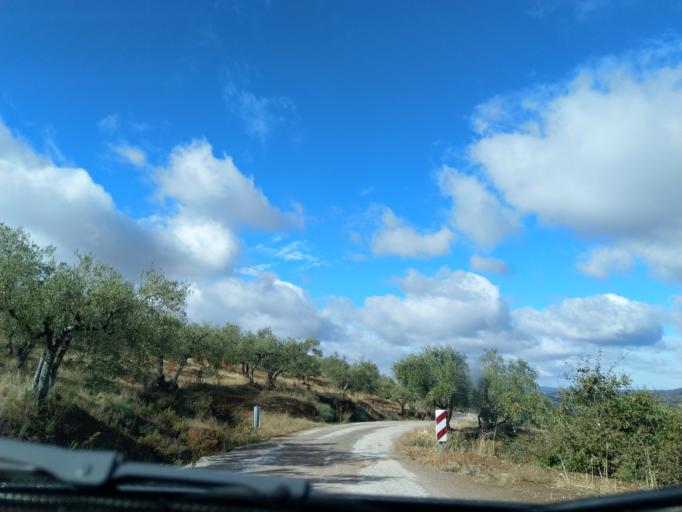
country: ES
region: Extremadura
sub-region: Provincia de Badajoz
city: Reina
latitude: 38.1289
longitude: -5.9250
